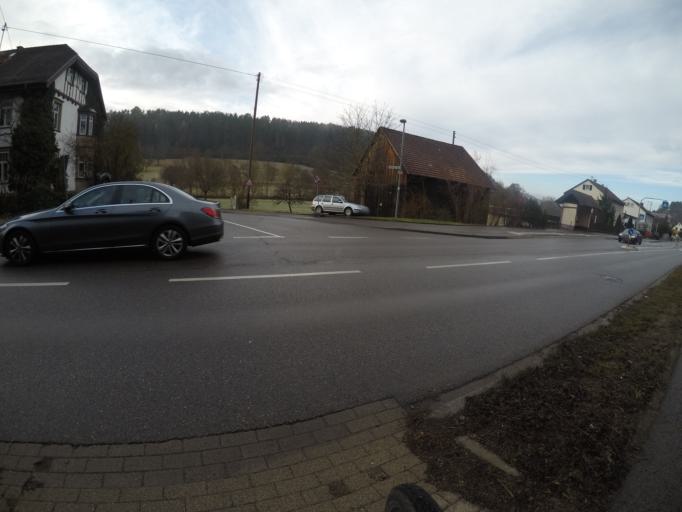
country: DE
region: Baden-Wuerttemberg
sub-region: Regierungsbezirk Stuttgart
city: Aidlingen
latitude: 48.6782
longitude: 8.8724
